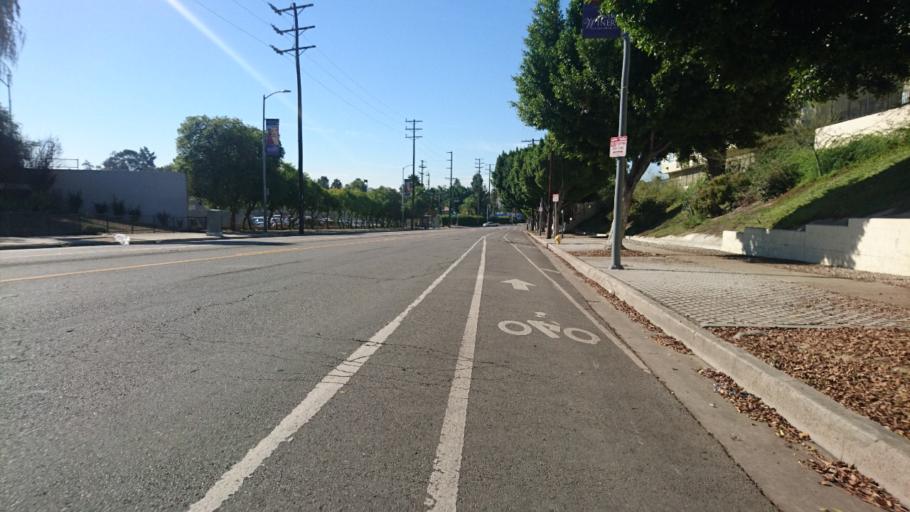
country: US
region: California
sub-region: Los Angeles County
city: Boyle Heights
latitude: 34.0716
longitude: -118.1982
